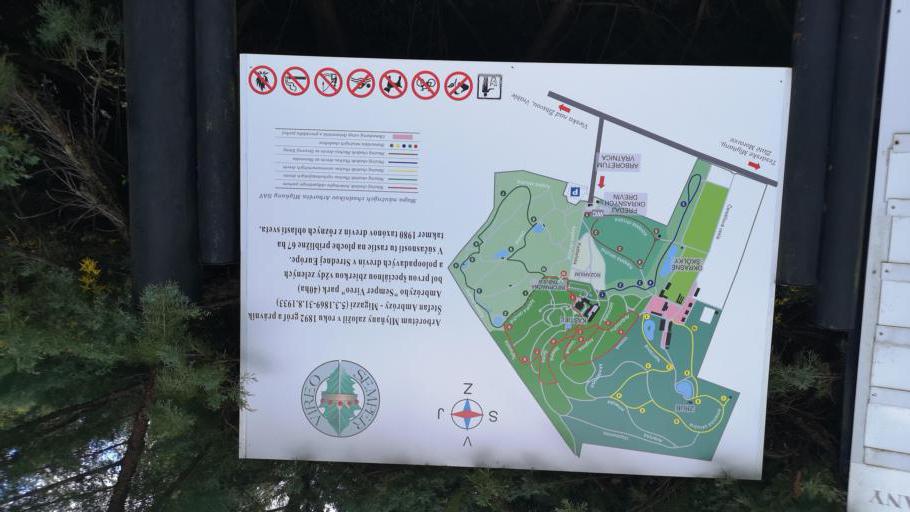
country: SK
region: Nitriansky
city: Zlate Moravce
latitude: 48.3193
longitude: 18.3648
